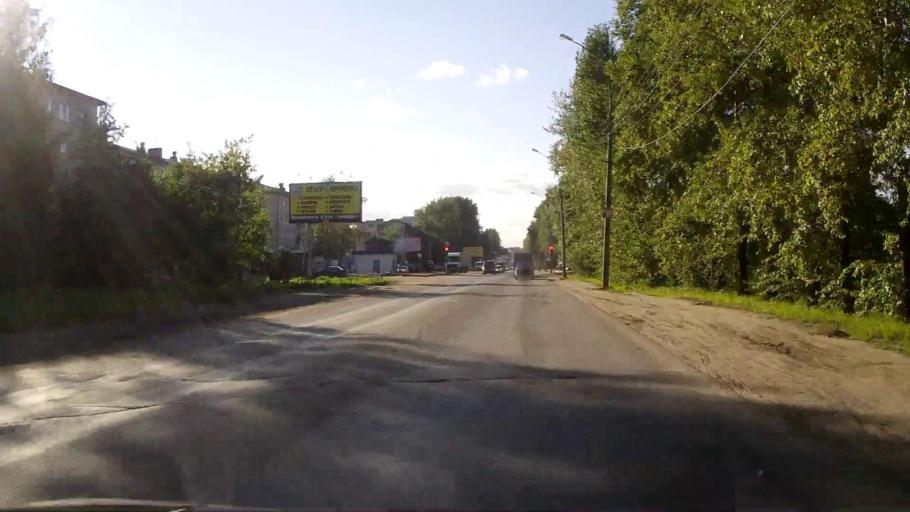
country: RU
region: Vologda
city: Vologda
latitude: 59.2052
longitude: 39.8648
